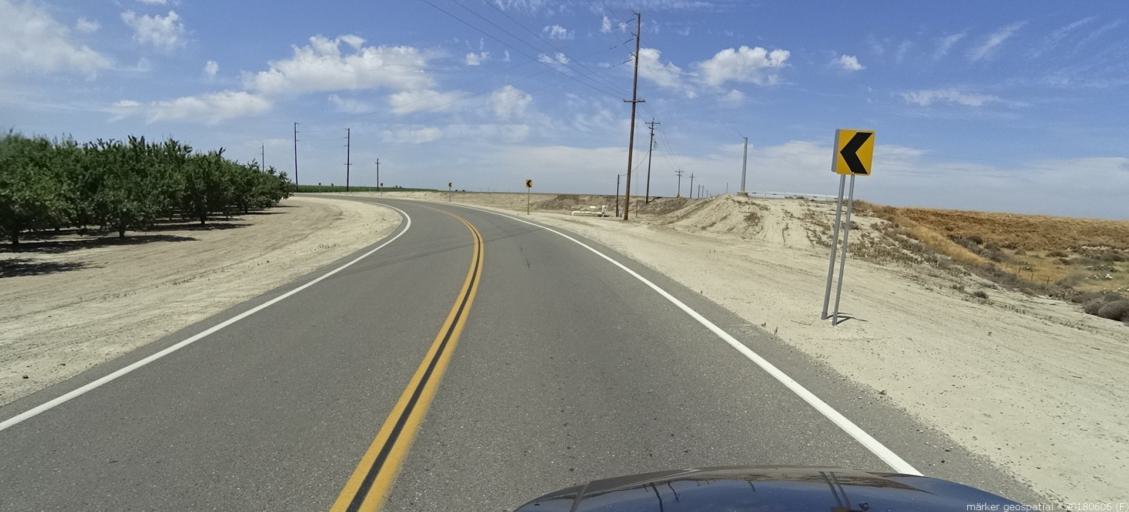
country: US
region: California
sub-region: Fresno County
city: Mendota
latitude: 36.8503
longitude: -120.3170
